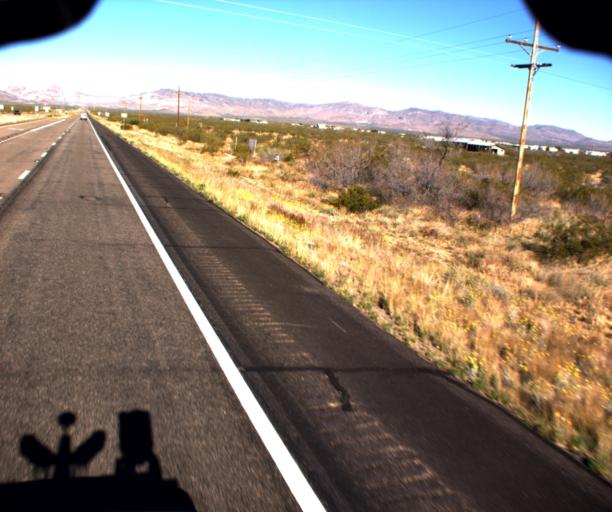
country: US
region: Arizona
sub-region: Mohave County
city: Golden Valley
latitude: 35.2258
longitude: -114.2913
